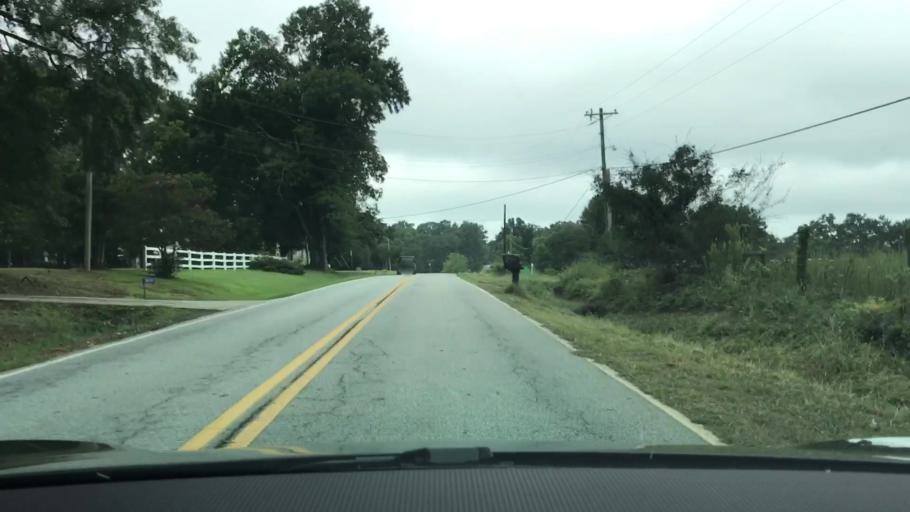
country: US
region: Georgia
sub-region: Barrow County
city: Auburn
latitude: 34.0669
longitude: -83.8383
